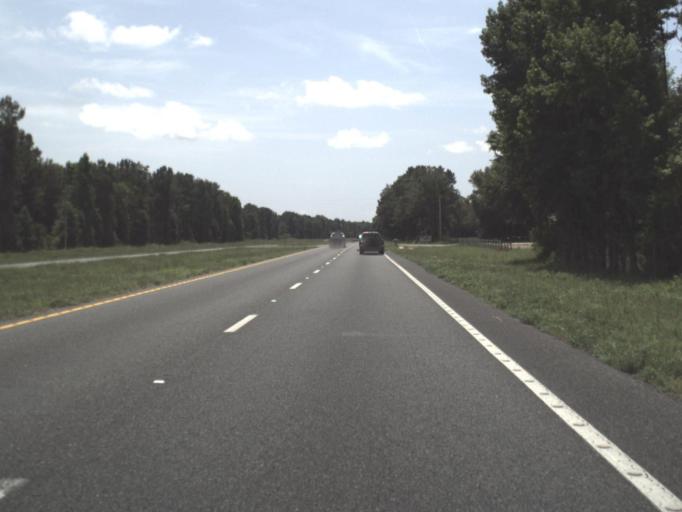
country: US
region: Florida
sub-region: Taylor County
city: Perry
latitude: 29.9984
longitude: -83.5060
